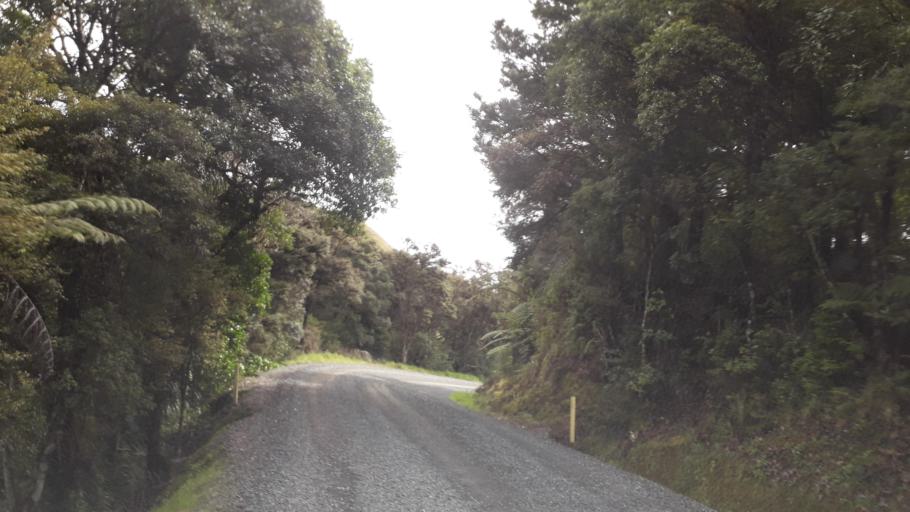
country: NZ
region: Northland
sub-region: Far North District
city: Taipa
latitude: -35.0951
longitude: 173.5336
